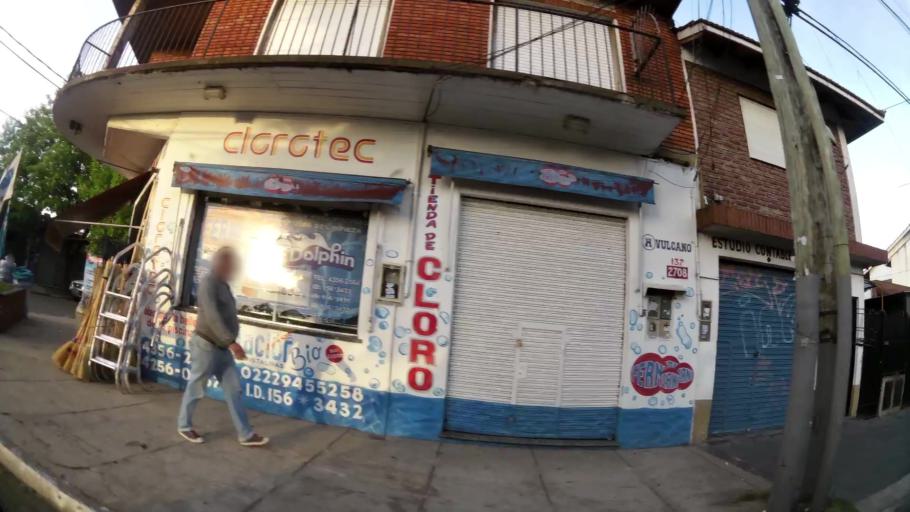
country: AR
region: Buenos Aires
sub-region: Partido de Quilmes
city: Quilmes
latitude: -34.7804
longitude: -58.2112
